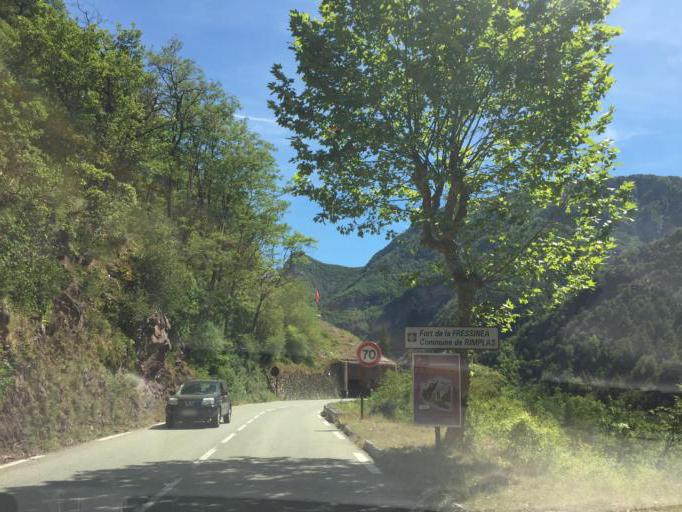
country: FR
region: Provence-Alpes-Cote d'Azur
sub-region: Departement des Alpes-Maritimes
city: Saint-Martin-Vesubie
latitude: 44.0636
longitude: 7.1171
